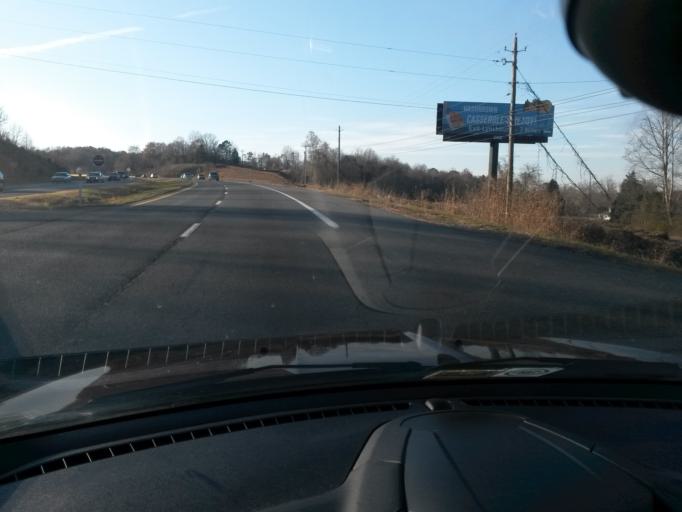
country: US
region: Virginia
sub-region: Amherst County
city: Madison Heights
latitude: 37.3864
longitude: -79.0750
